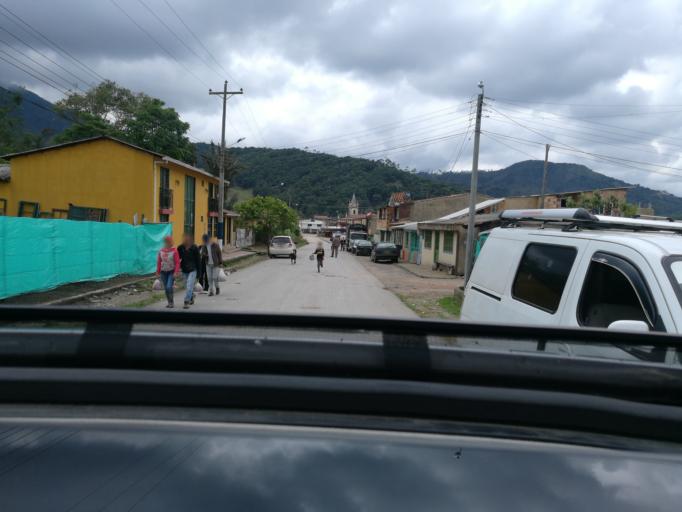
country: CO
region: Boyaca
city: Arcabuco
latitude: 5.7567
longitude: -73.4337
